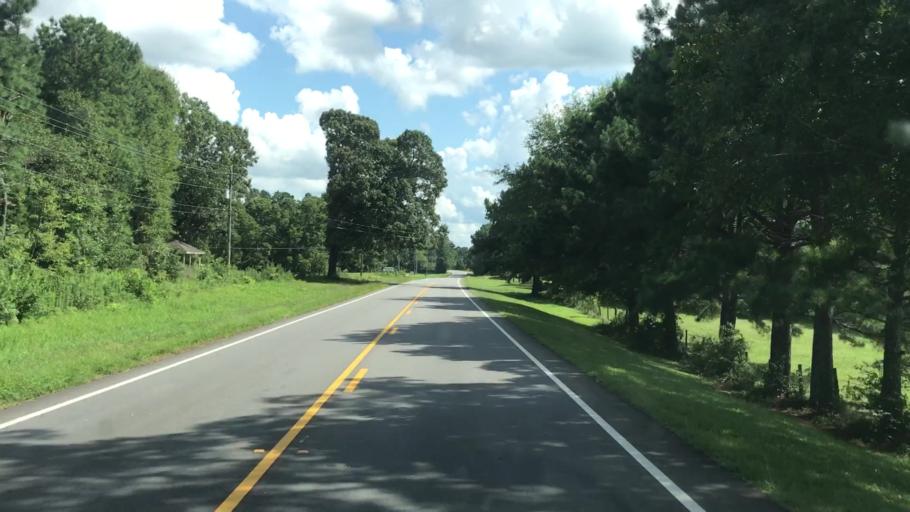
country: US
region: Georgia
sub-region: Newton County
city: Oxford
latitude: 33.6622
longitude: -83.8508
